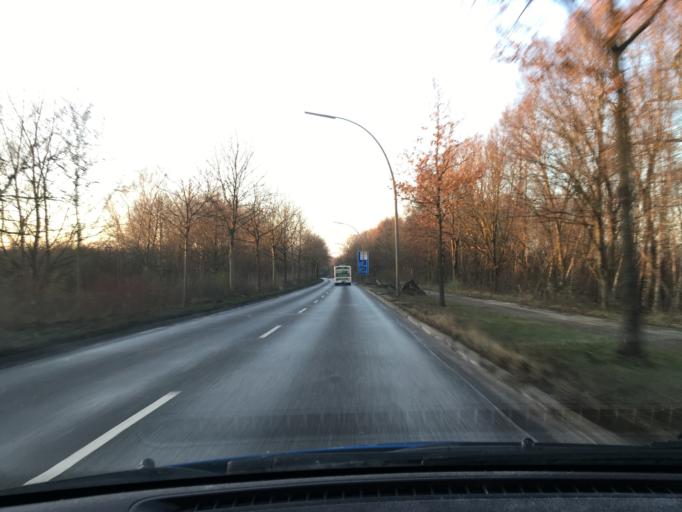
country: DE
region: Hamburg
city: Harburg
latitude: 53.4797
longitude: 9.9221
